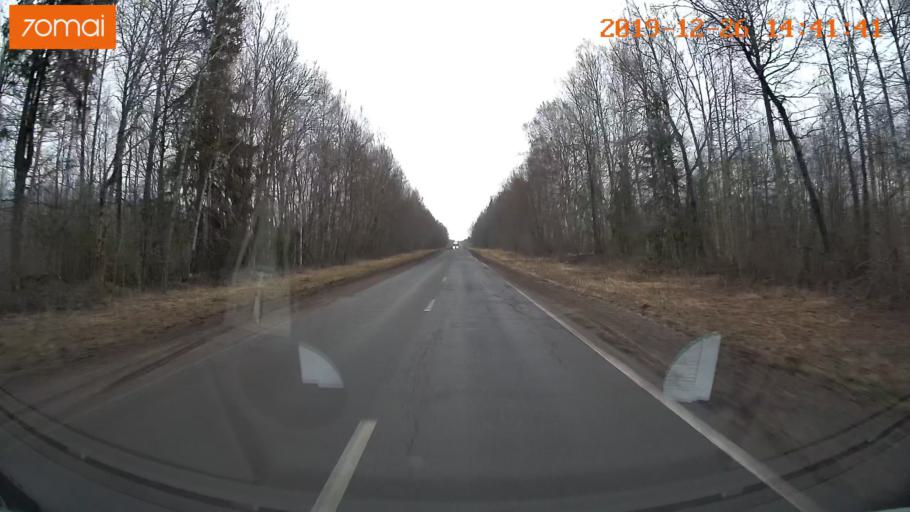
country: RU
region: Jaroslavl
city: Poshekhon'ye
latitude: 58.3692
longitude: 39.0224
